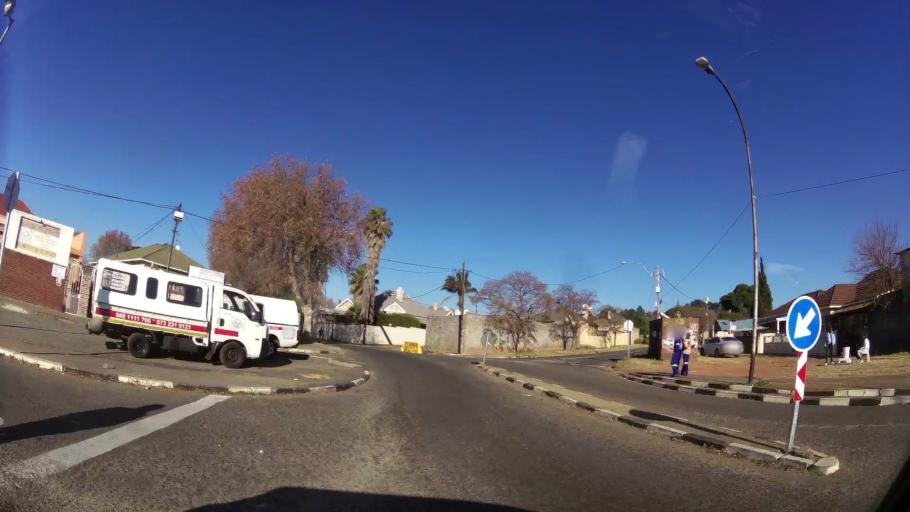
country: ZA
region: Gauteng
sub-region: City of Johannesburg Metropolitan Municipality
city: Johannesburg
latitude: -26.1977
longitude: 28.1129
